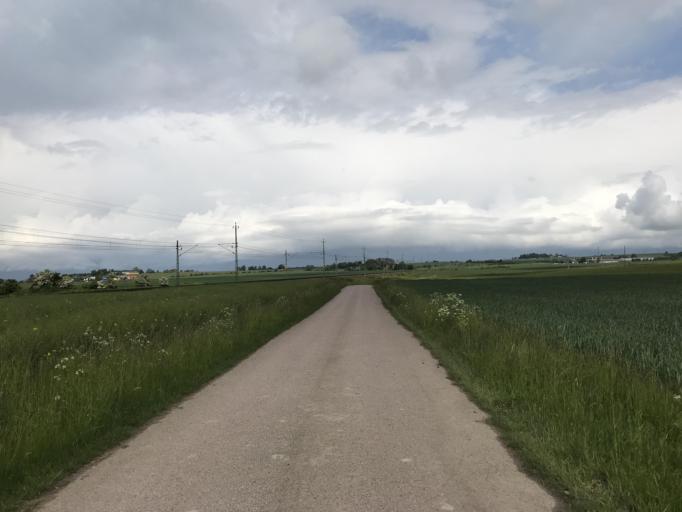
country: SE
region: Skane
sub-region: Landskrona
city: Landskrona
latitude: 55.9089
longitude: 12.8433
